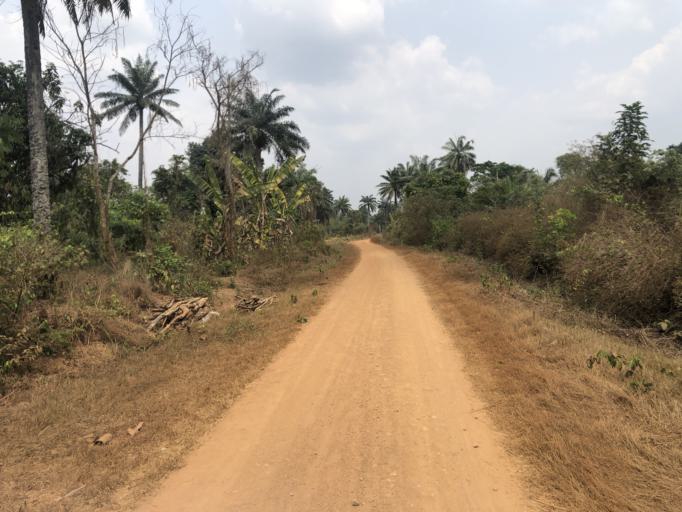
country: NG
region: Osun
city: Bode Osi
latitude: 7.7573
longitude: 4.2670
